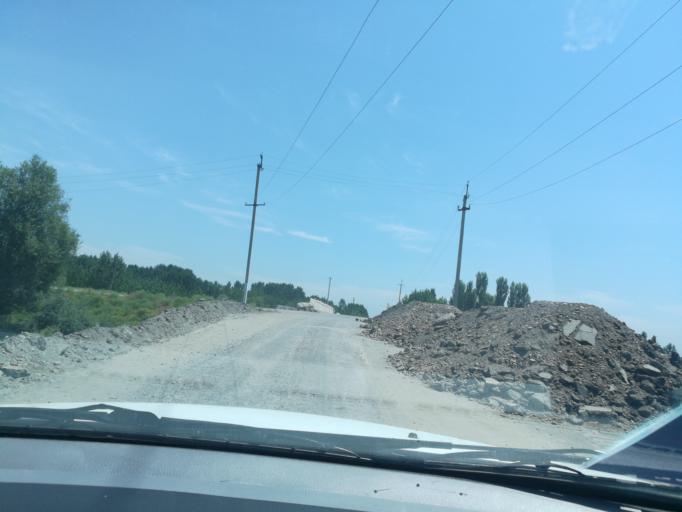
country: UZ
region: Namangan
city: Haqqulobod
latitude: 40.8993
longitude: 72.0028
